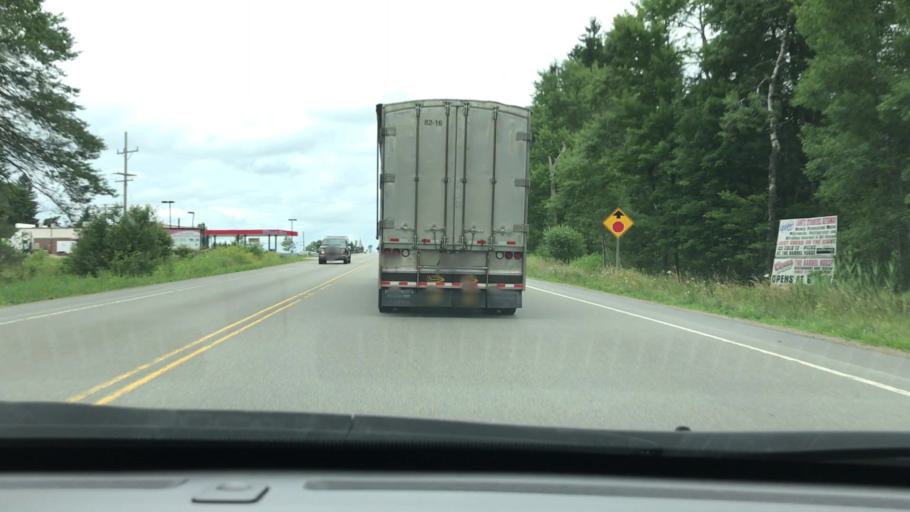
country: US
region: Pennsylvania
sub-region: McKean County
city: Kane
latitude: 41.7057
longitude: -78.6933
